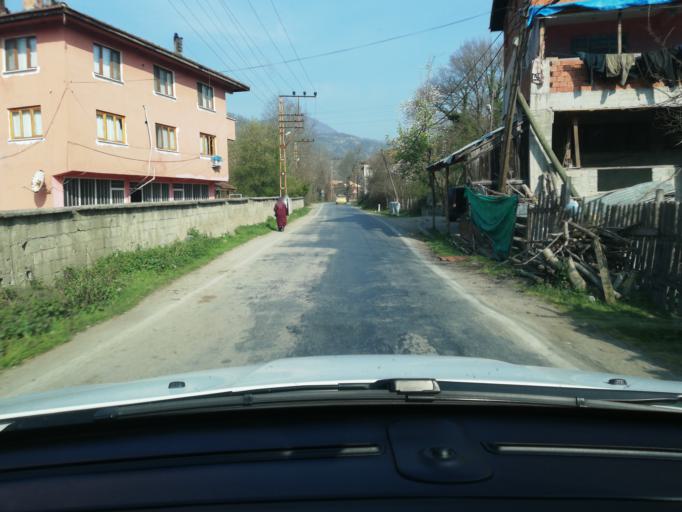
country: TR
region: Karabuk
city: Yenice
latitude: 41.2113
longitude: 32.3652
